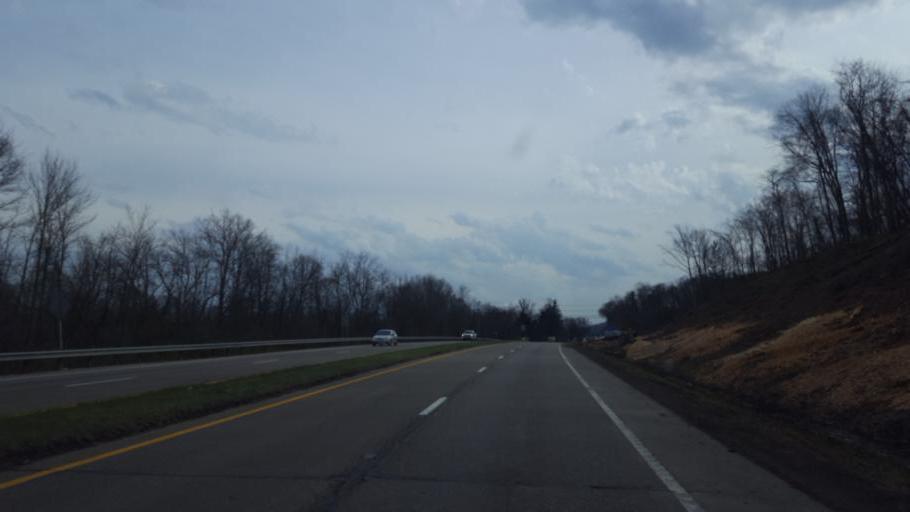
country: US
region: Ohio
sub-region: Coshocton County
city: Coshocton
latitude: 40.2496
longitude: -81.8731
